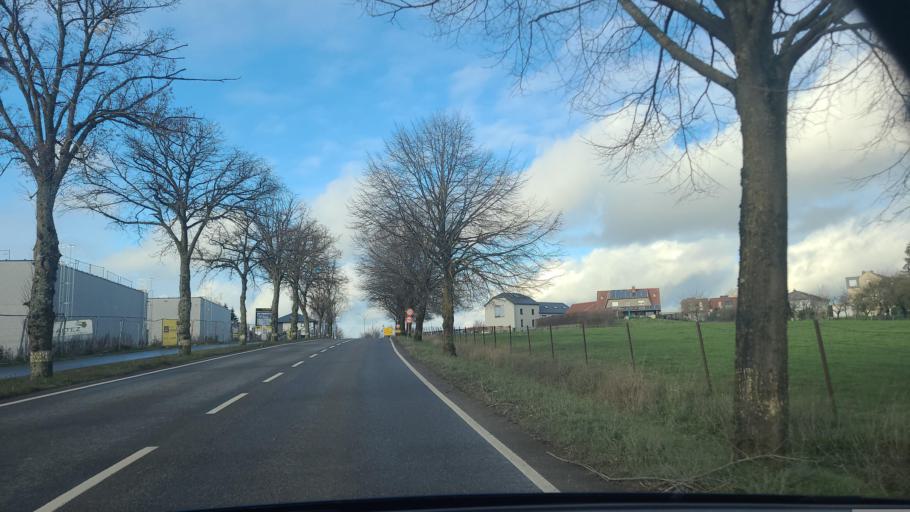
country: LU
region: Luxembourg
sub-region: Canton de Capellen
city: Dippach
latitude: 49.5855
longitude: 5.9735
